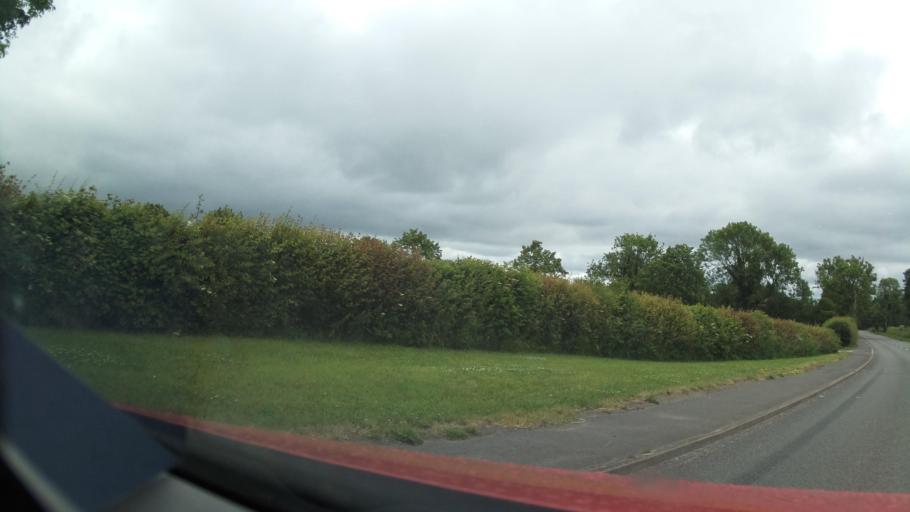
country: GB
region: England
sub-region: Derbyshire
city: Rodsley
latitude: 52.8779
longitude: -1.6987
